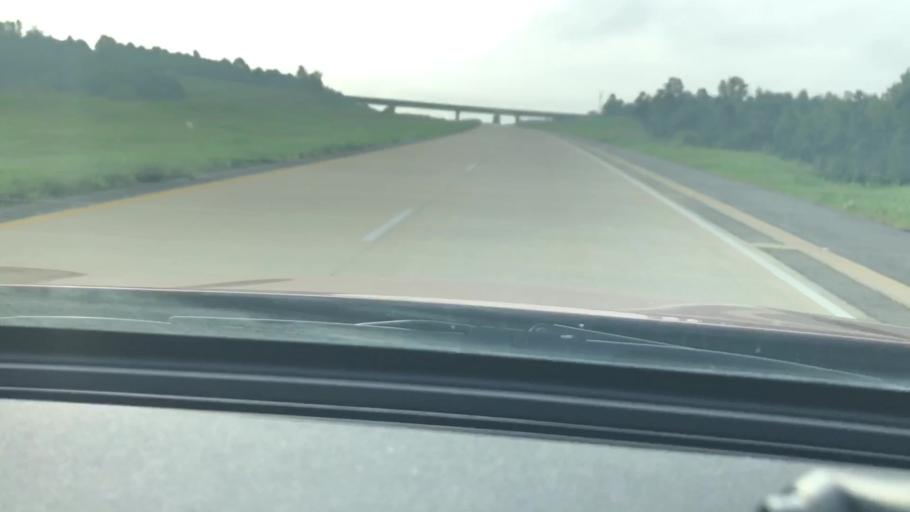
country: US
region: Louisiana
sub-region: Caddo Parish
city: Vivian
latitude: 32.9256
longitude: -93.8910
